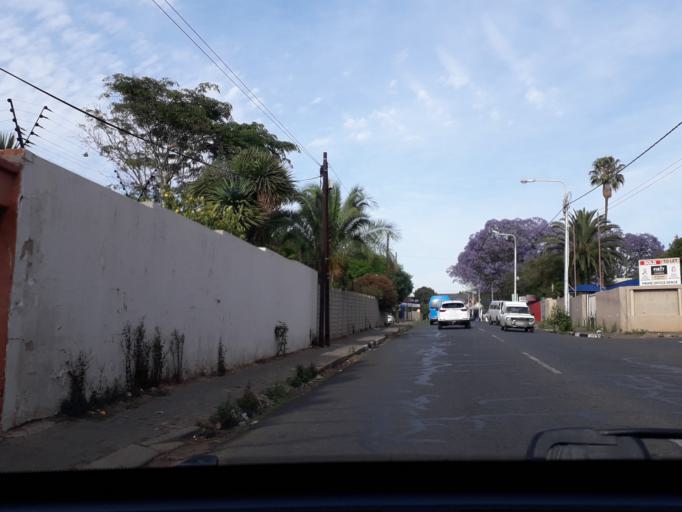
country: ZA
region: Gauteng
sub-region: City of Johannesburg Metropolitan Municipality
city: Johannesburg
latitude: -26.1495
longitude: 28.0937
